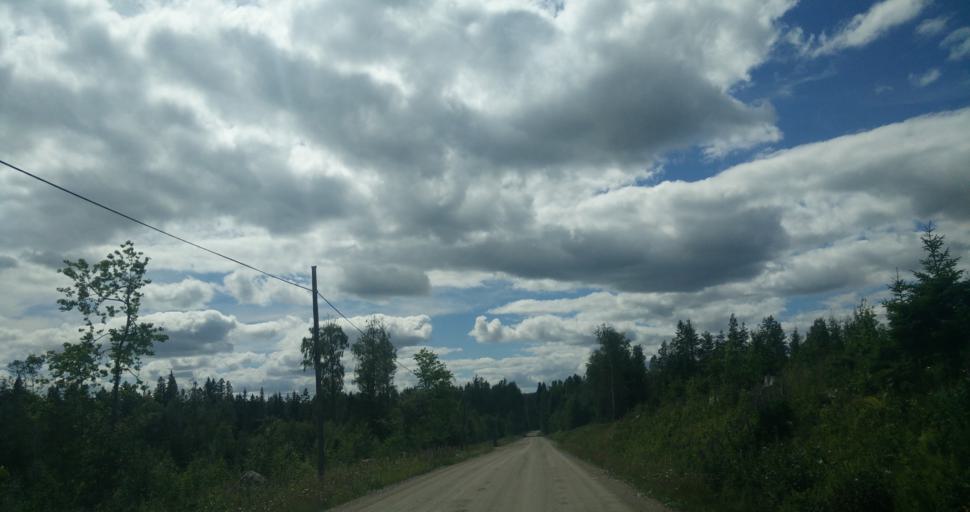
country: SE
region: Gaevleborg
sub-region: Nordanstigs Kommun
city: Bergsjoe
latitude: 62.1321
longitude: 17.1299
